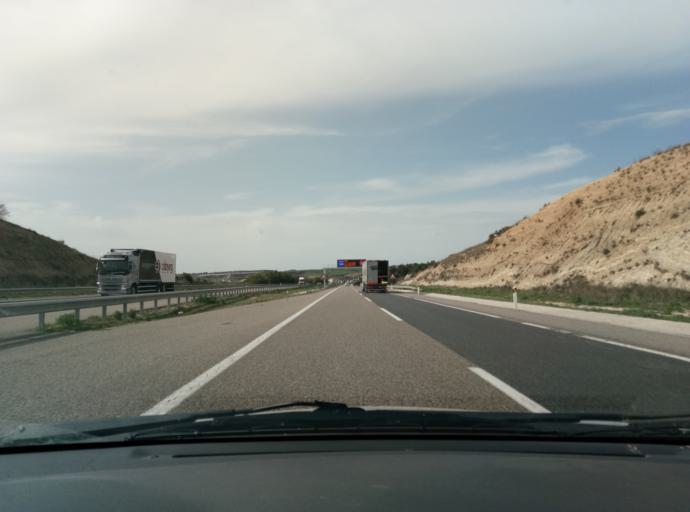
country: ES
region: Catalonia
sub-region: Provincia de Lleida
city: Cervera
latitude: 41.6533
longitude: 1.3148
